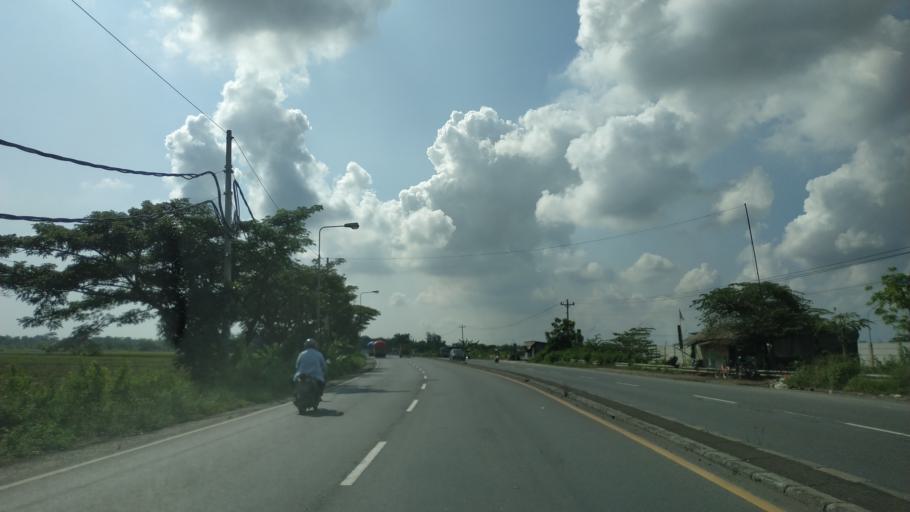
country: ID
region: Central Java
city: Wiradesa
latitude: -6.8883
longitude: 109.5780
